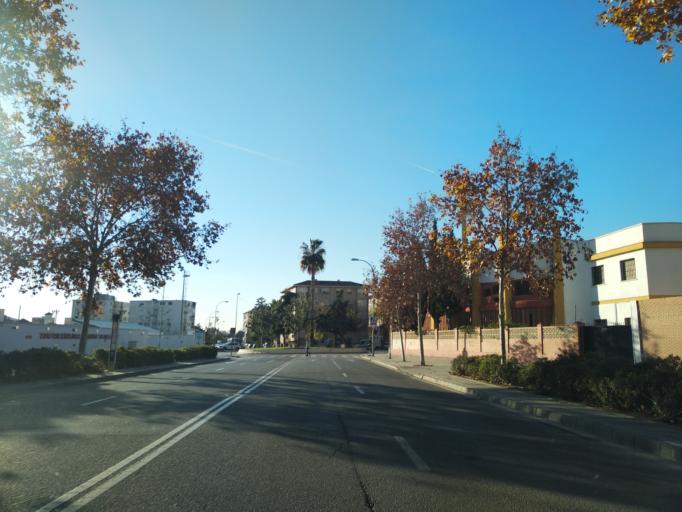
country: ES
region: Andalusia
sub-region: Provincia de Malaga
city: Malaga
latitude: 36.7423
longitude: -4.4266
